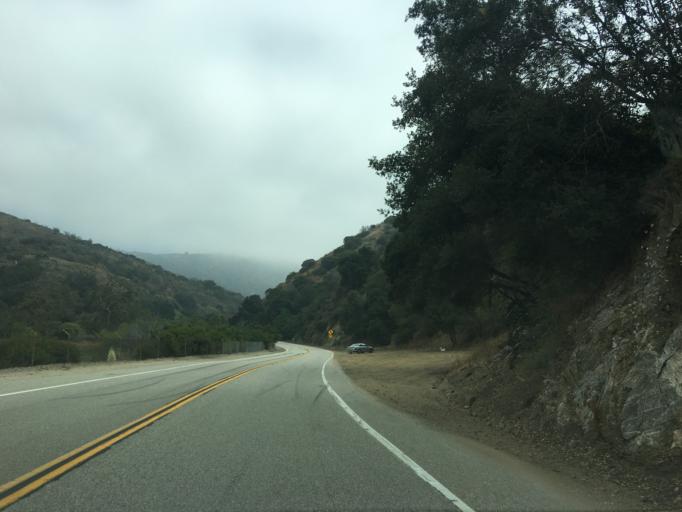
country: US
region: California
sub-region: Los Angeles County
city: Glendora
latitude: 34.1601
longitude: -117.8384
